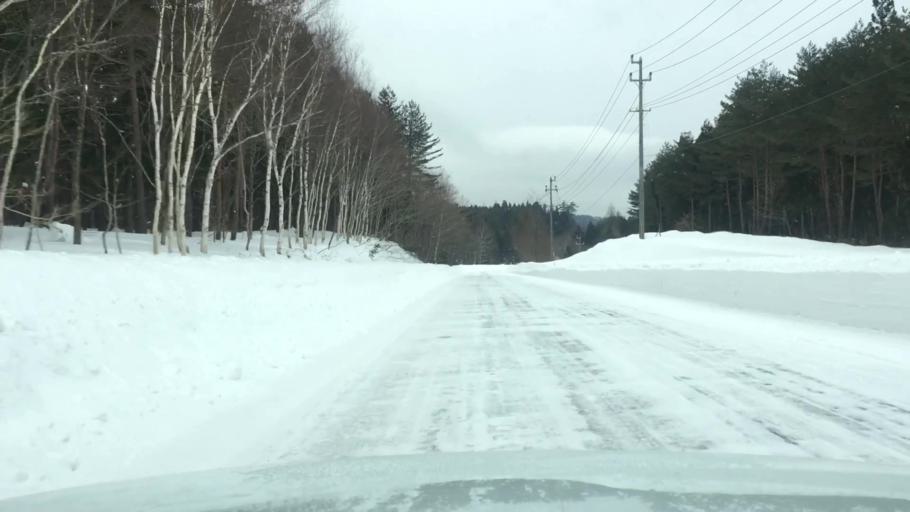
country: JP
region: Akita
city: Hanawa
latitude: 39.9878
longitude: 140.9989
